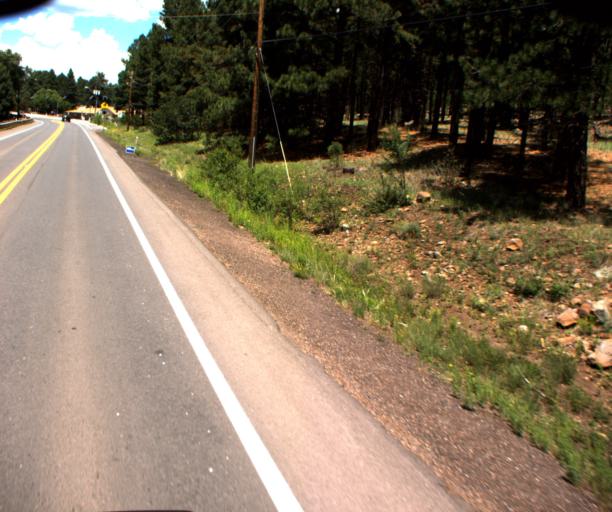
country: US
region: Arizona
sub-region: Coconino County
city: Flagstaff
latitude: 35.2207
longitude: -111.6519
